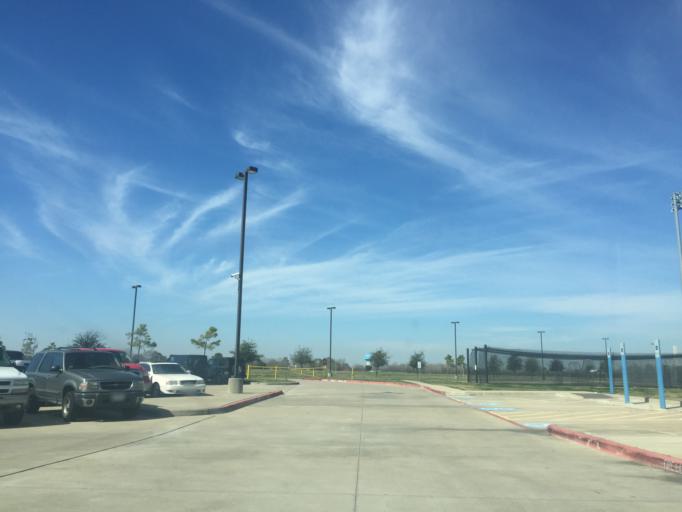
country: US
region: Texas
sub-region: Galveston County
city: Kemah
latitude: 29.5112
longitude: -95.0250
